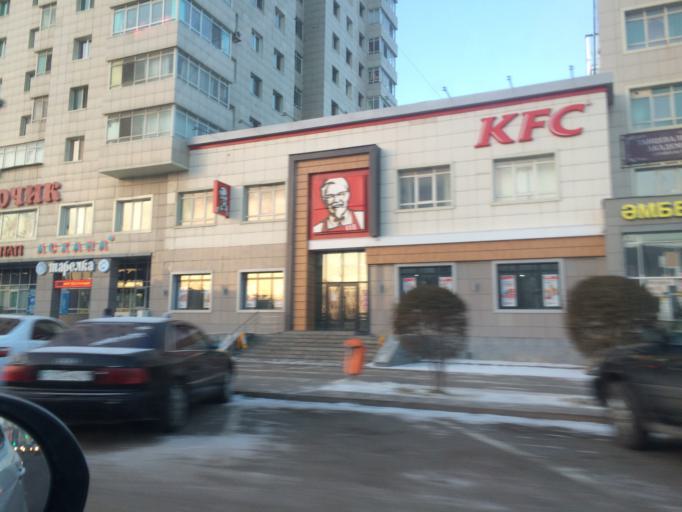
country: KZ
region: Astana Qalasy
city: Astana
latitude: 51.1860
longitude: 71.4081
